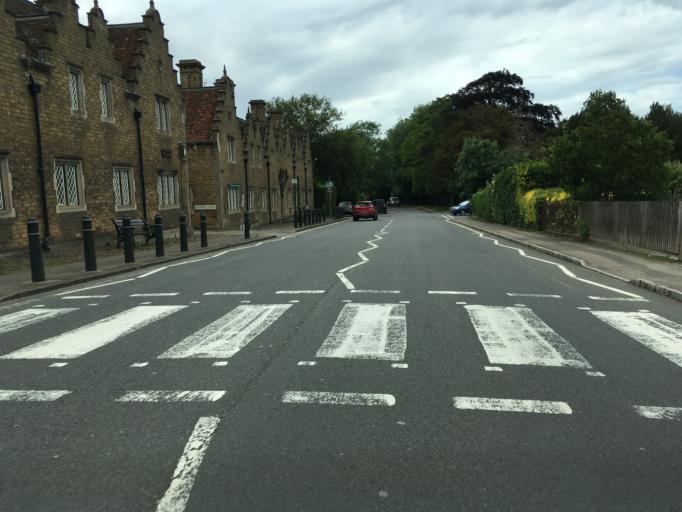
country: GB
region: England
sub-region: Central Bedfordshire
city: Woburn
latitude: 51.9908
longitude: -0.6205
